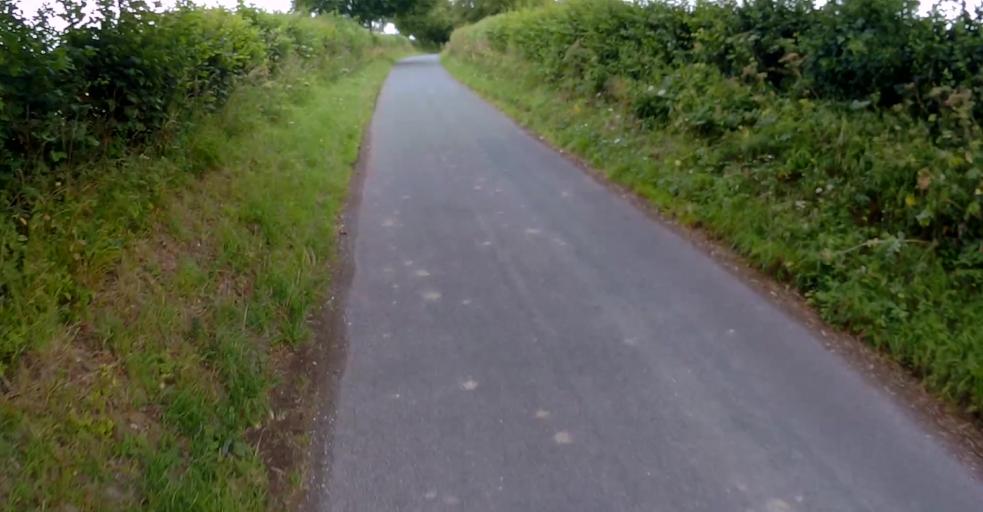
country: GB
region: England
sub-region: Hampshire
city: Kings Worthy
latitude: 51.0736
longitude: -1.2050
